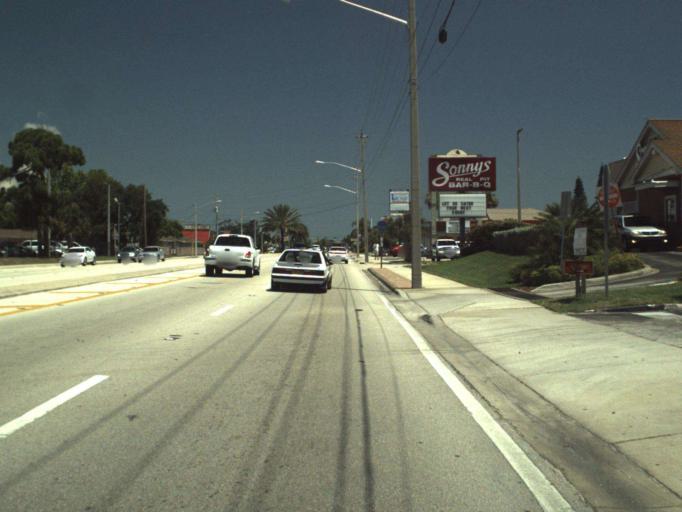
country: US
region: Florida
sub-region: Brevard County
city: Rockledge
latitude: 28.3617
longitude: -80.7001
